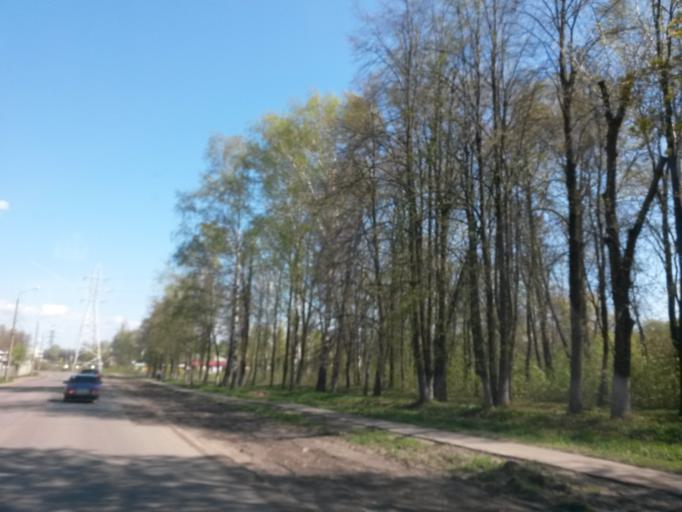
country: RU
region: Jaroslavl
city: Yaroslavl
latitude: 57.5856
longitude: 39.8751
